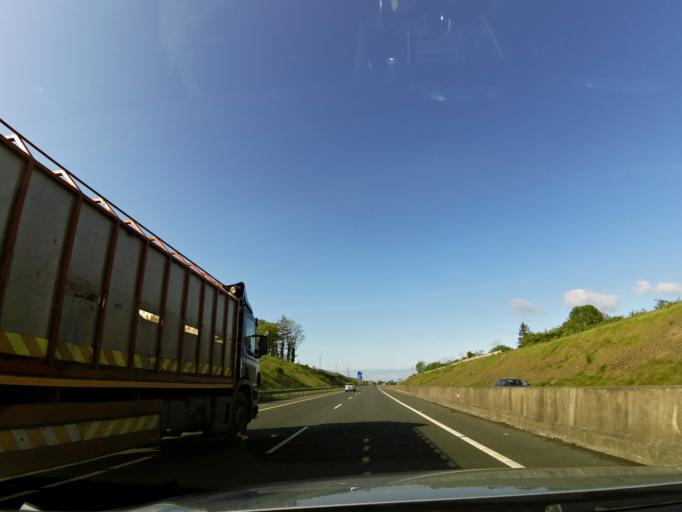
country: IE
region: Munster
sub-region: North Tipperary
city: Newport
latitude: 52.7651
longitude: -8.3922
